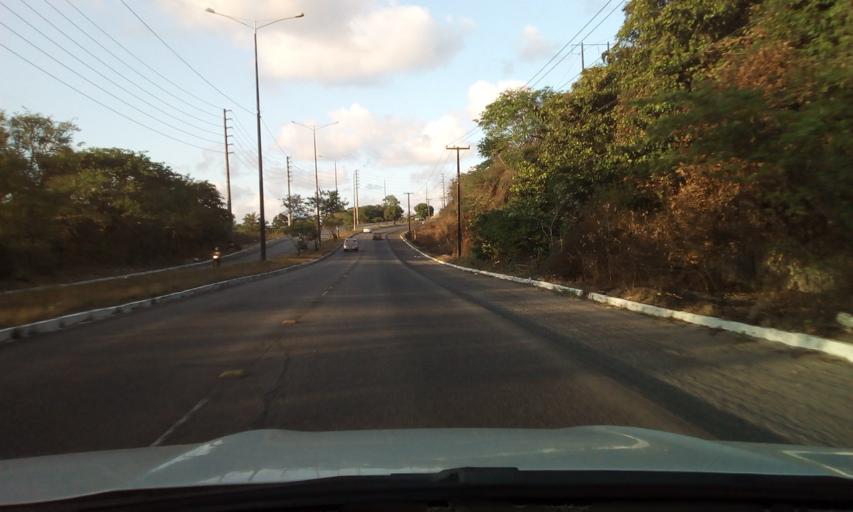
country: BR
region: Paraiba
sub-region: Bayeux
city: Bayeux
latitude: -7.1348
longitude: -34.9051
